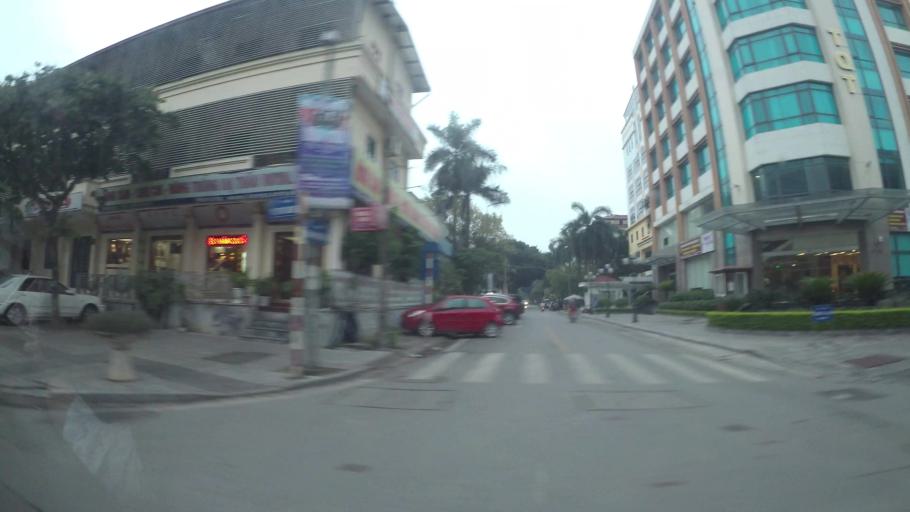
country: VN
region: Ha Noi
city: Hanoi
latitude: 21.0215
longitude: 105.8433
